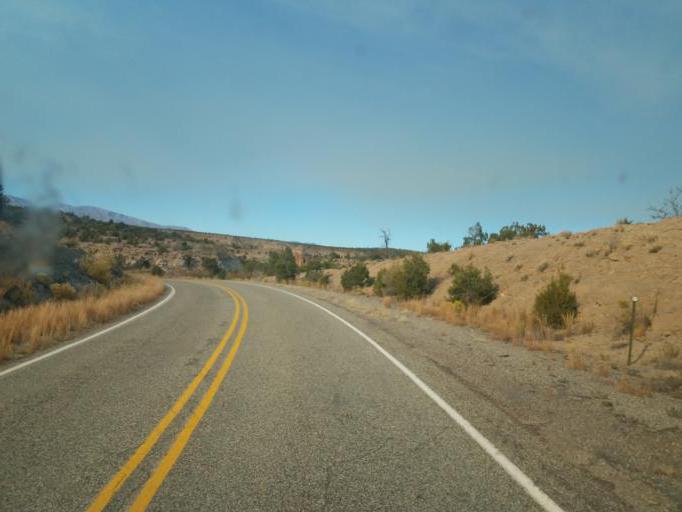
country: US
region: New Mexico
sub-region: Los Alamos County
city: White Rock
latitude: 35.7982
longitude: -106.2454
